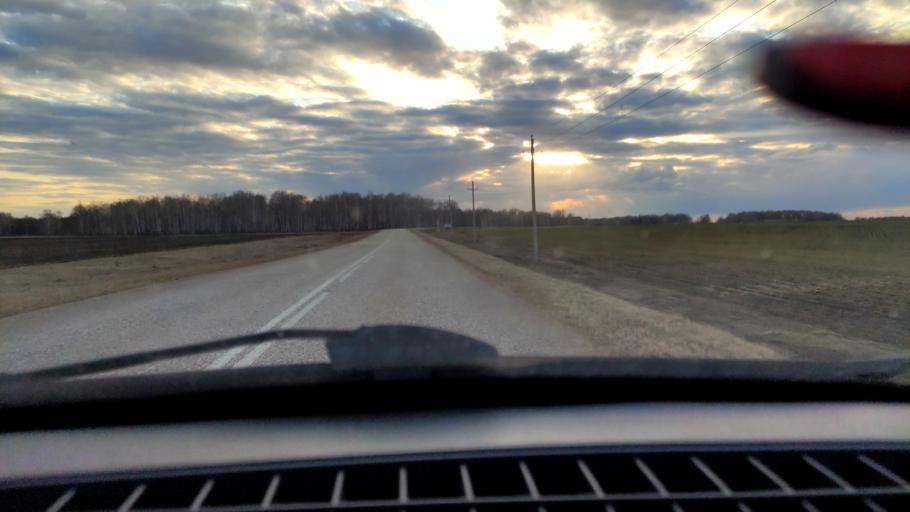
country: RU
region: Bashkortostan
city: Tolbazy
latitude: 54.0039
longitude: 55.6202
